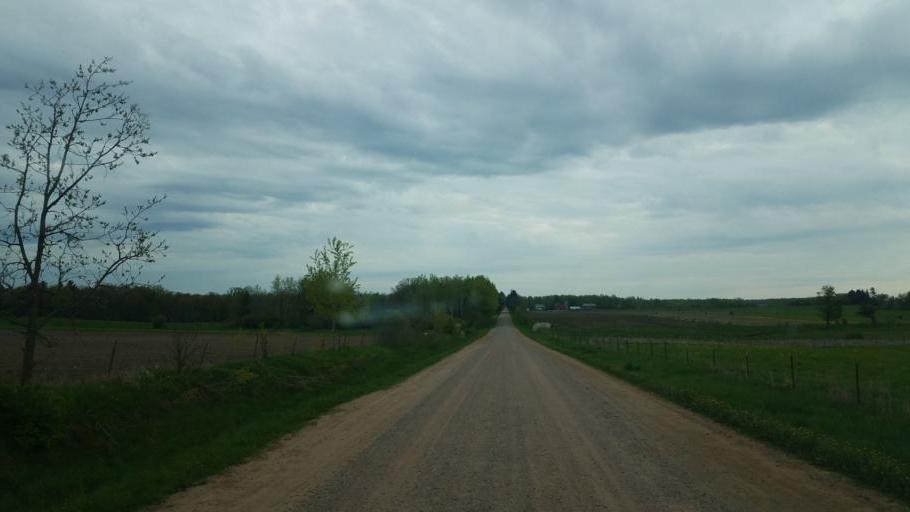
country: US
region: Wisconsin
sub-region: Marathon County
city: Spencer
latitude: 44.6012
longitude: -90.3765
